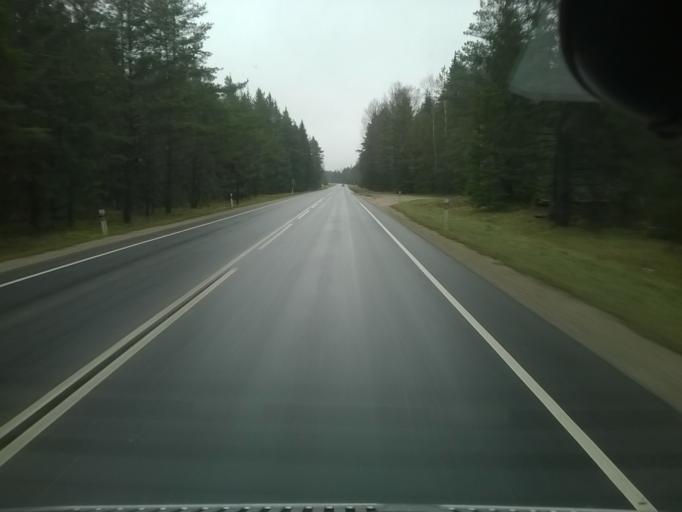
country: EE
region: Harju
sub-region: Nissi vald
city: Turba
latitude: 59.0312
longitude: 24.1575
